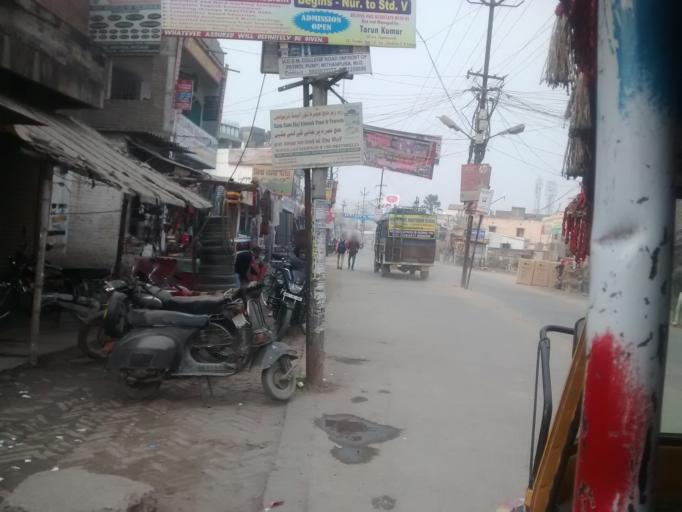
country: IN
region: Bihar
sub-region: Muzaffarpur
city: Muzaffarpur
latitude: 26.1045
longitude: 85.3990
